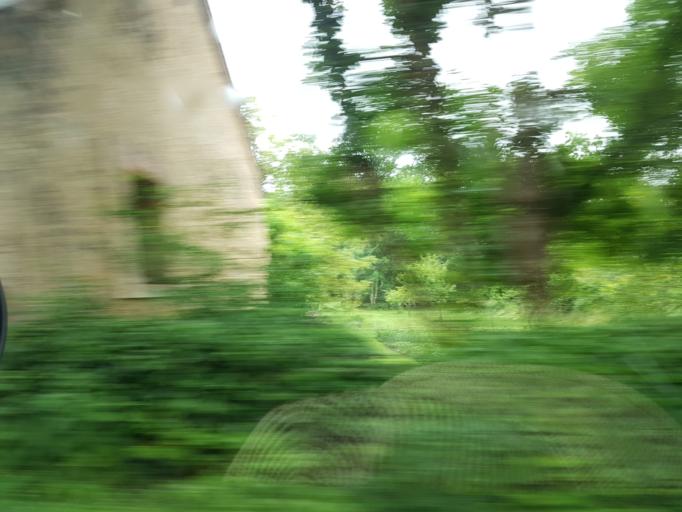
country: FR
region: Bourgogne
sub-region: Departement de la Nievre
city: Corbigny
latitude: 47.1766
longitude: 3.7443
